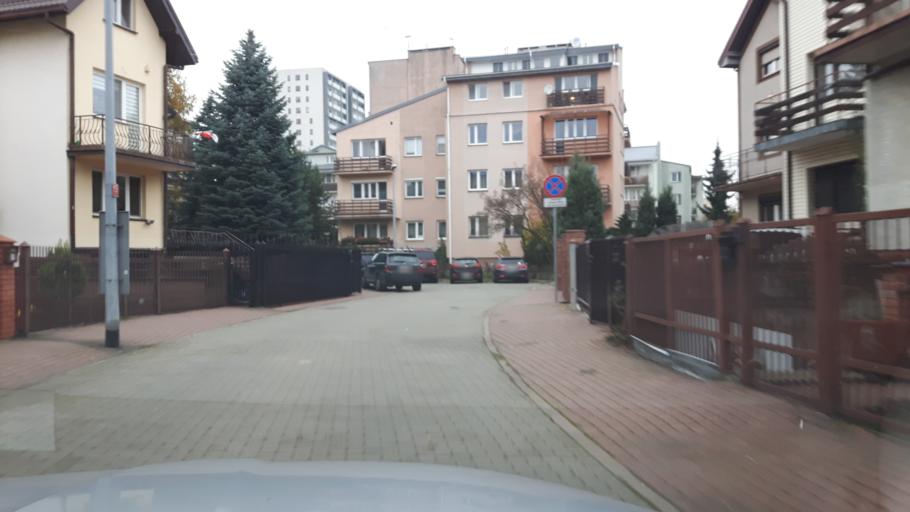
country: PL
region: Masovian Voivodeship
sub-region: Warszawa
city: Targowek
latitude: 52.2910
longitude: 21.0556
